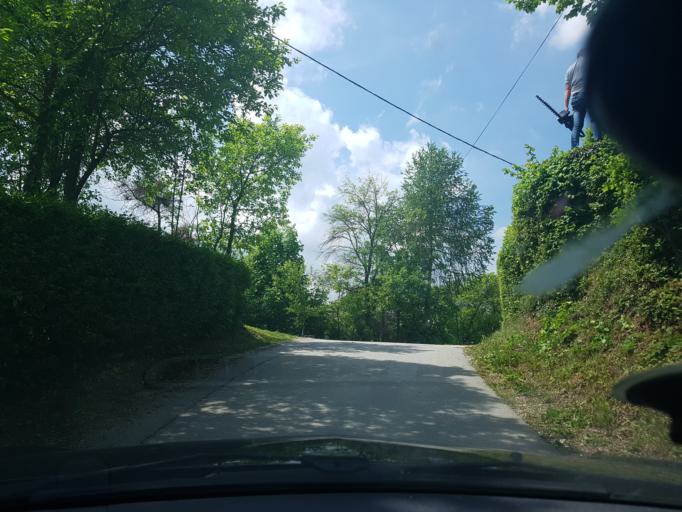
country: SI
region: Rogatec
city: Rogatec
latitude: 46.2156
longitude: 15.7054
